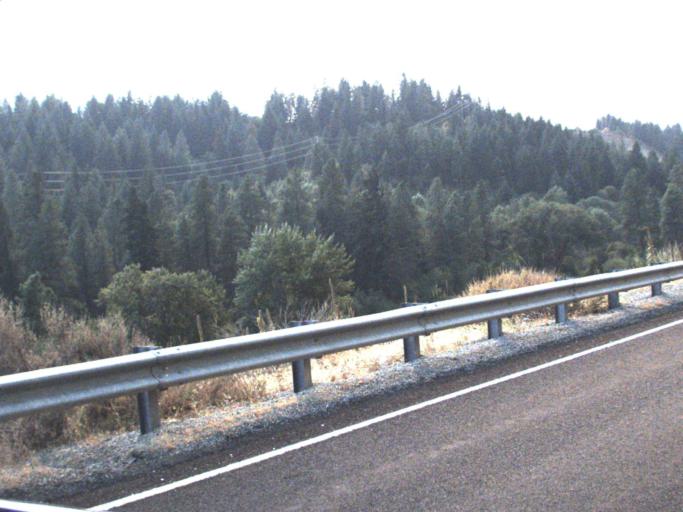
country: US
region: Washington
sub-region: Kittitas County
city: Cle Elum
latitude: 47.1654
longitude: -120.8166
